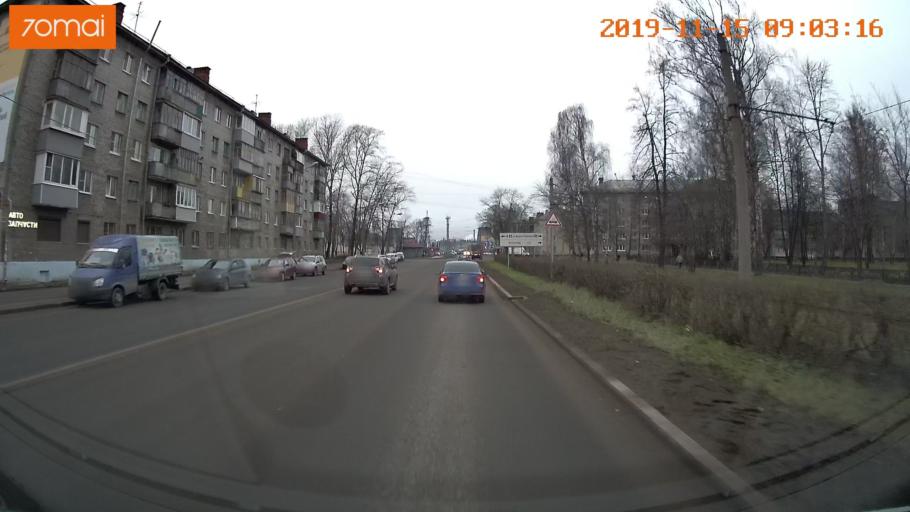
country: RU
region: Vologda
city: Cherepovets
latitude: 59.1380
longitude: 37.9229
